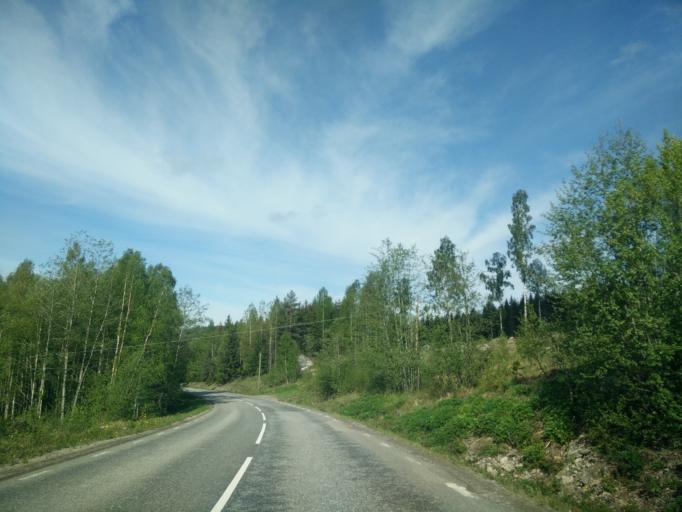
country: SE
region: Vaesternorrland
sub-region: Sundsvalls Kommun
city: Nolby
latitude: 62.3046
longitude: 17.2862
